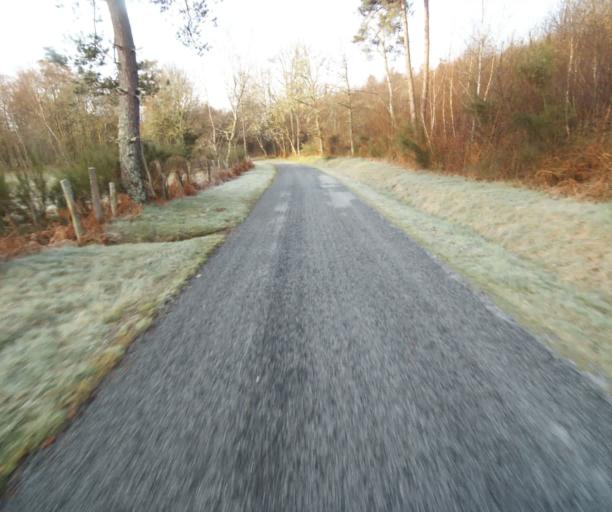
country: FR
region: Limousin
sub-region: Departement de la Correze
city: Correze
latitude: 45.3179
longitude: 1.8603
